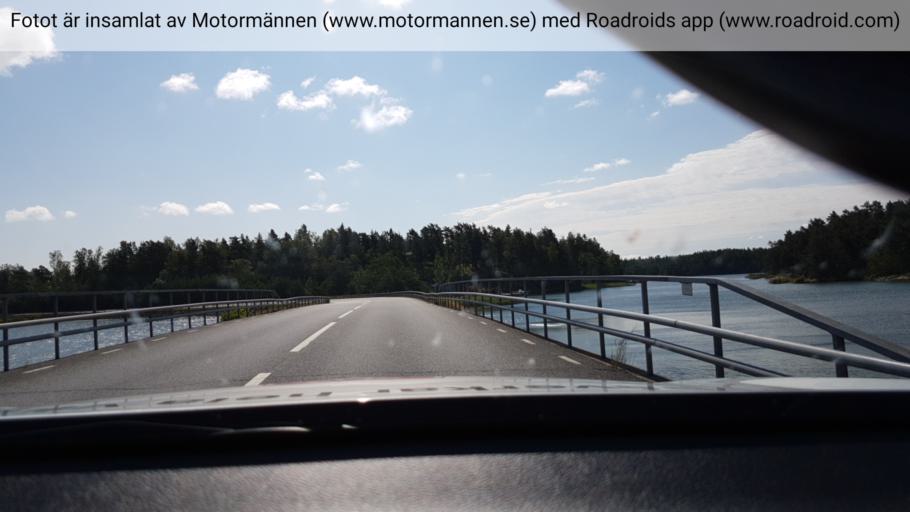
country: SE
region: Stockholm
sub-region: Norrtalje Kommun
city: Norrtalje
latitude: 59.6806
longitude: 18.8074
